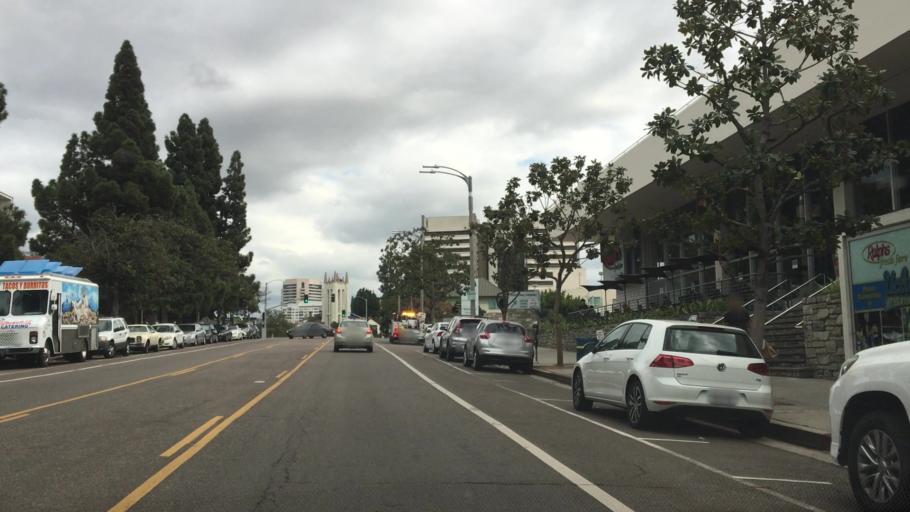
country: US
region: California
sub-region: Los Angeles County
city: Westwood, Los Angeles
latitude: 34.0637
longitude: -118.4442
